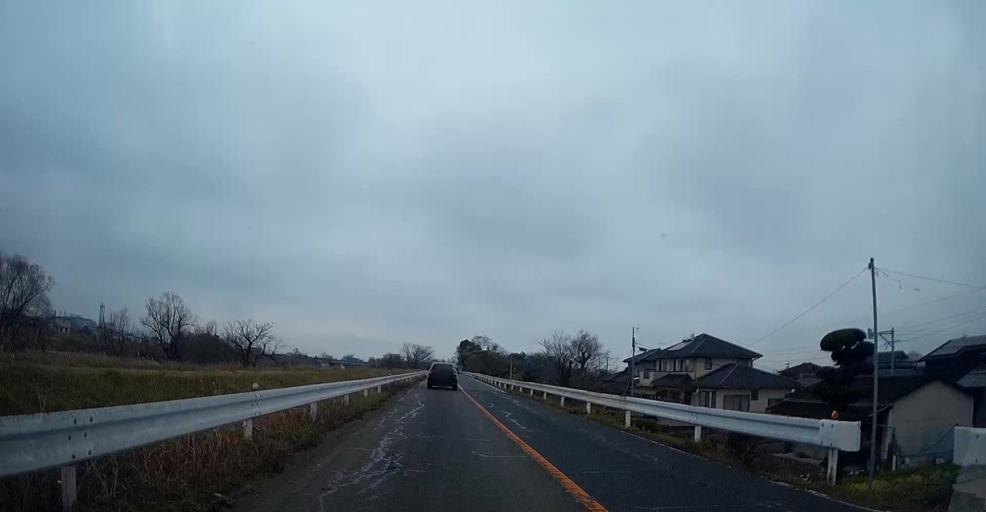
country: JP
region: Kumamoto
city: Kumamoto
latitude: 32.7538
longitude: 130.7445
